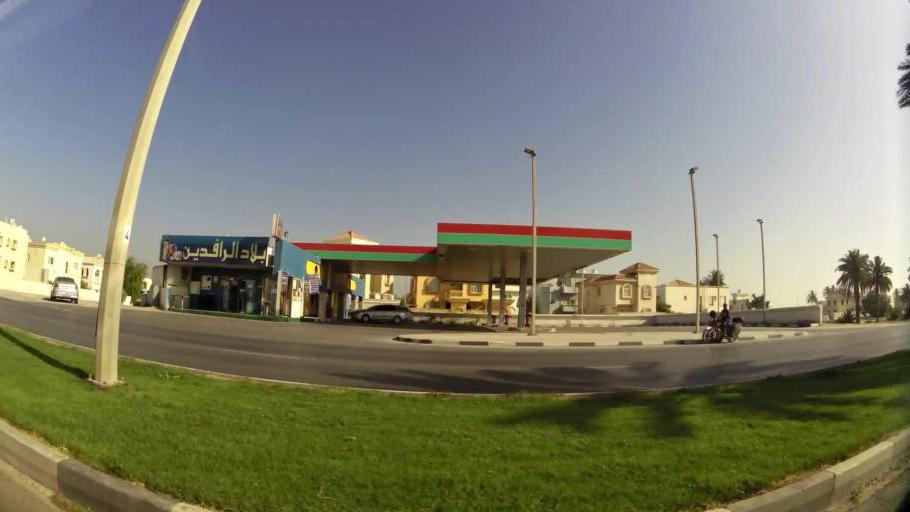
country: AE
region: Ajman
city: Ajman
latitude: 25.3849
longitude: 55.4099
